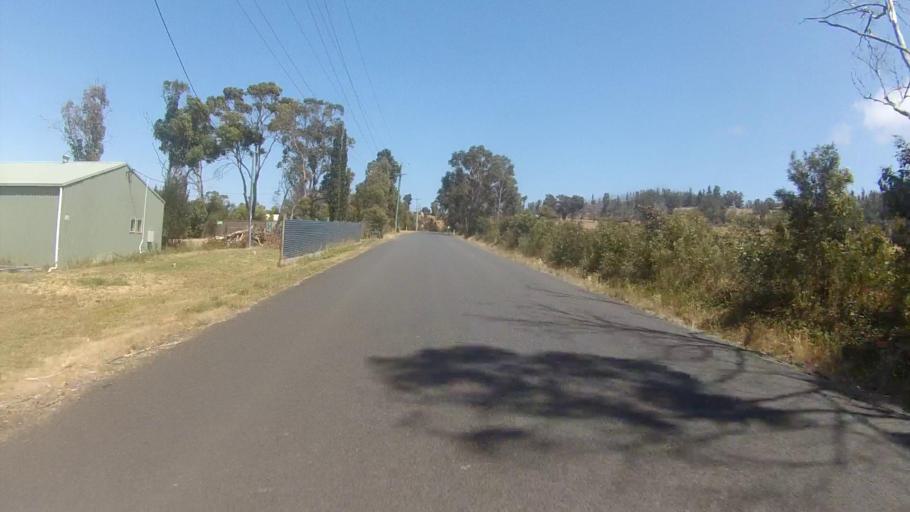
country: AU
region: Tasmania
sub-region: Sorell
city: Sorell
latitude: -42.8690
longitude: 147.8275
